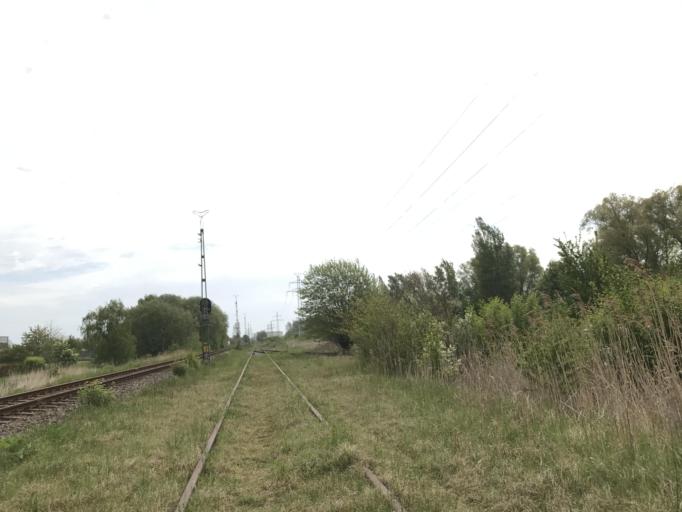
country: SE
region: Skane
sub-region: Landskrona
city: Landskrona
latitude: 55.8687
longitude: 12.8586
